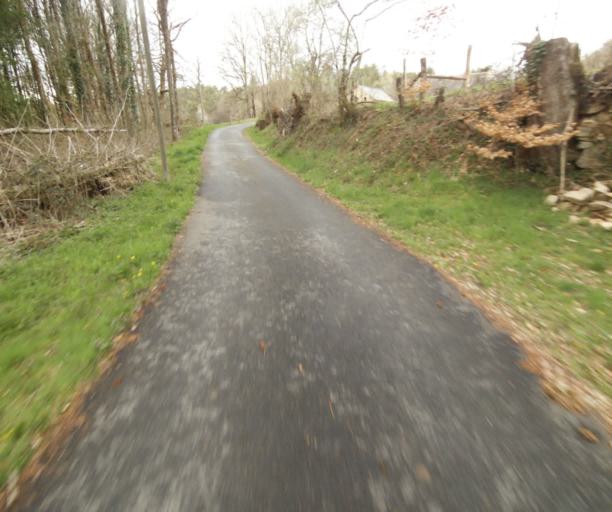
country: FR
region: Limousin
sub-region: Departement de la Correze
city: Argentat
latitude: 45.2011
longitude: 1.9821
